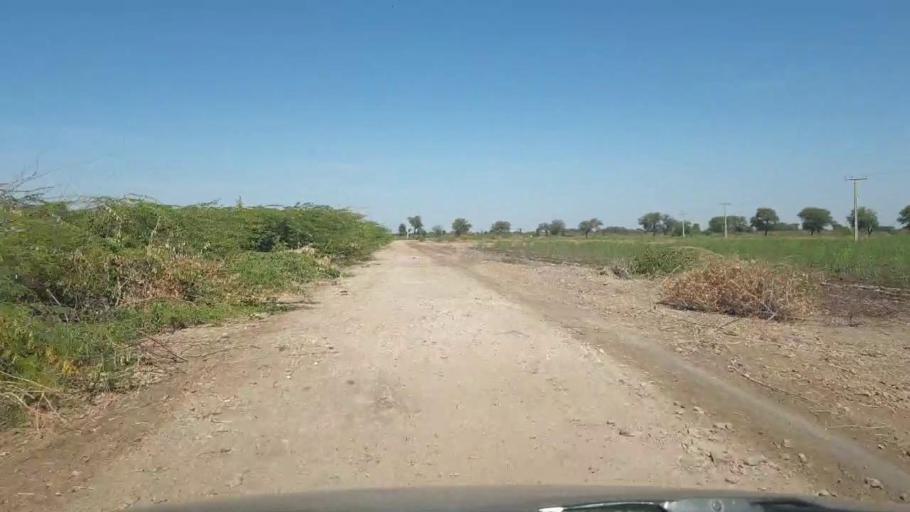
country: PK
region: Sindh
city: Dhoro Naro
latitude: 25.4223
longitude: 69.6195
